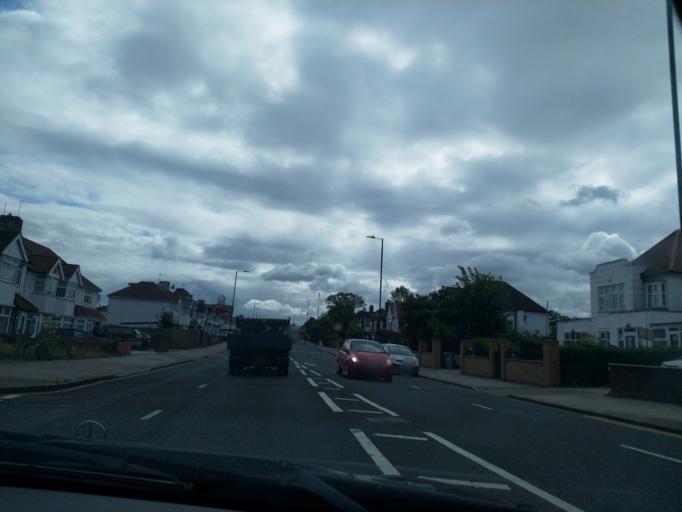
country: GB
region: England
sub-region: Greater London
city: Edgware
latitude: 51.5861
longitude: -0.2900
